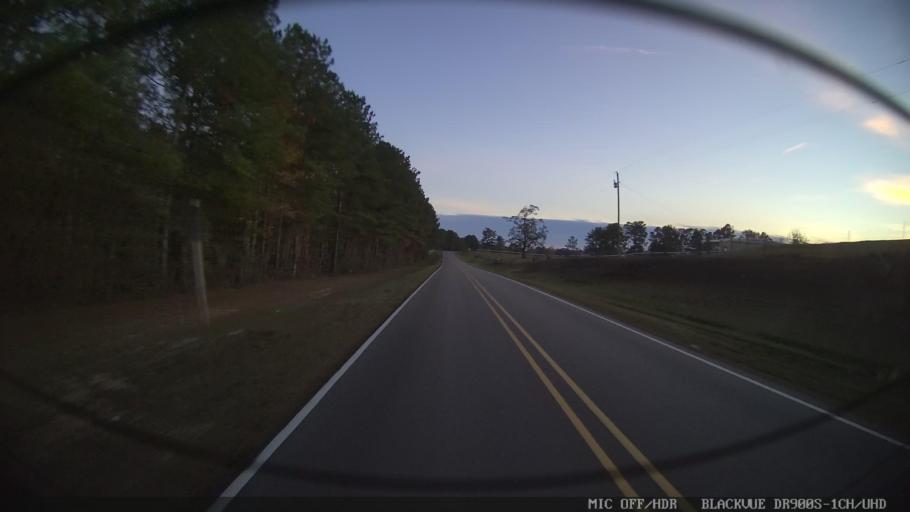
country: US
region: Mississippi
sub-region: Perry County
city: New Augusta
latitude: 31.0737
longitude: -89.1855
